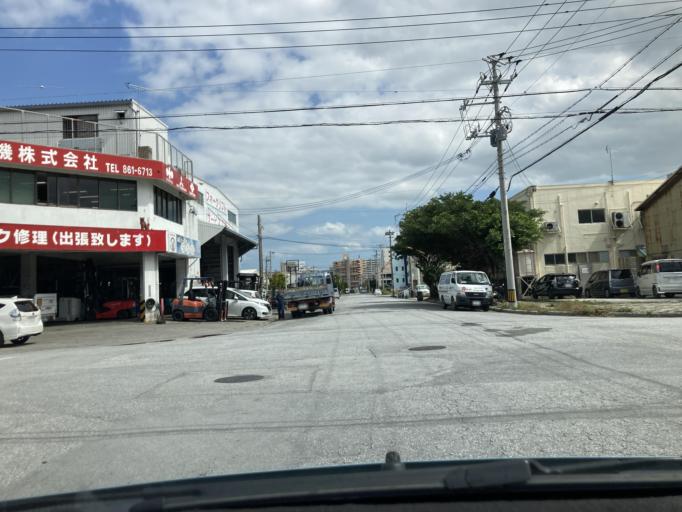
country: JP
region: Okinawa
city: Naha-shi
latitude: 26.2427
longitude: 127.6753
